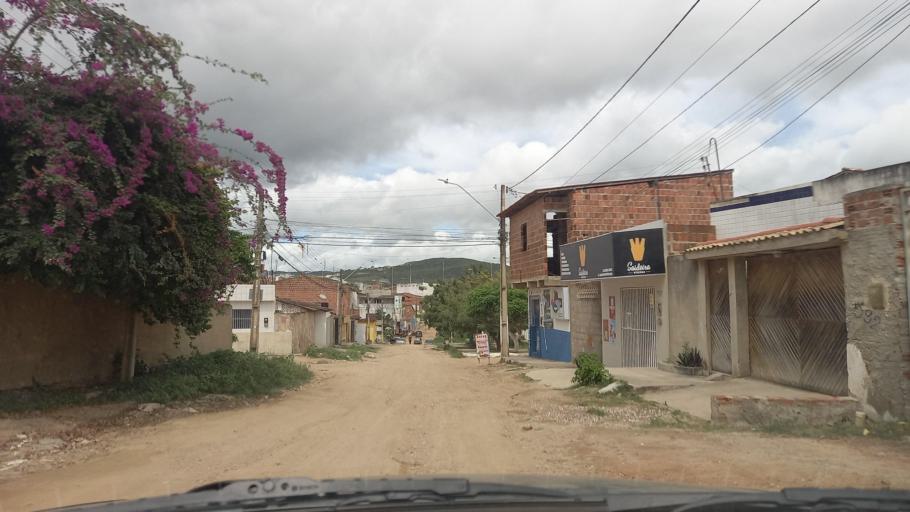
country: BR
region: Pernambuco
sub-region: Gravata
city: Gravata
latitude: -8.1943
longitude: -35.5777
